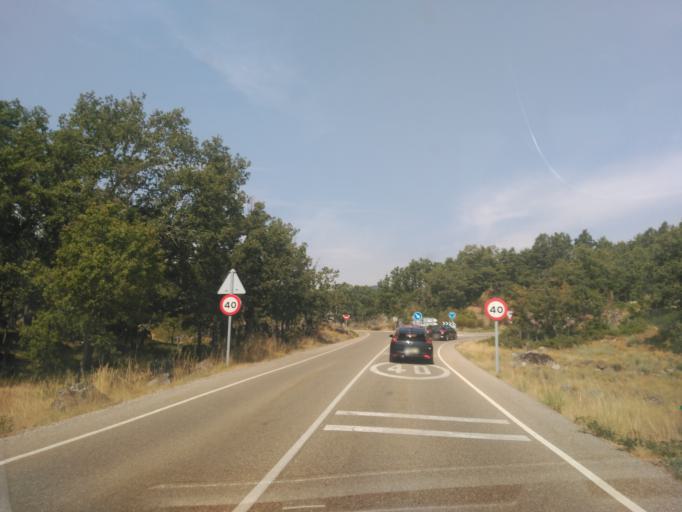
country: ES
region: Castille and Leon
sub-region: Provincia de Zamora
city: Galende
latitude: 42.1166
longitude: -6.6882
